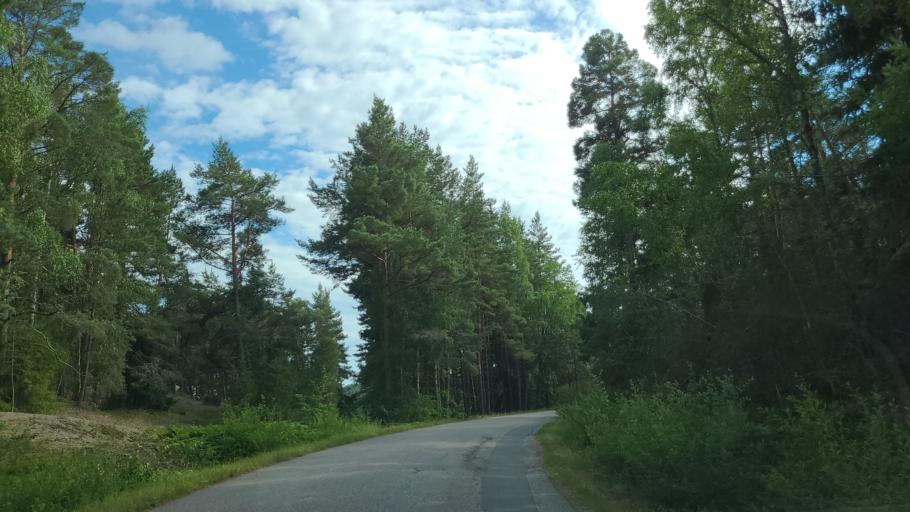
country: FI
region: Varsinais-Suomi
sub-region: Turku
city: Rymaettylae
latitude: 60.3016
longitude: 21.9425
